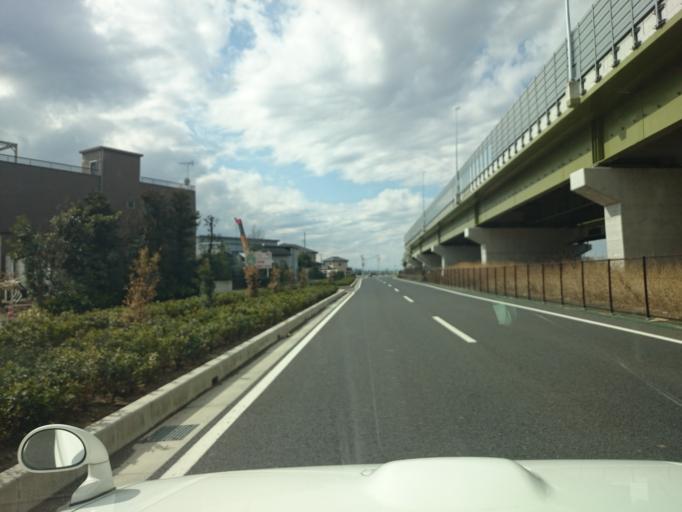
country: JP
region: Saitama
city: Satte
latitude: 36.0626
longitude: 139.7329
